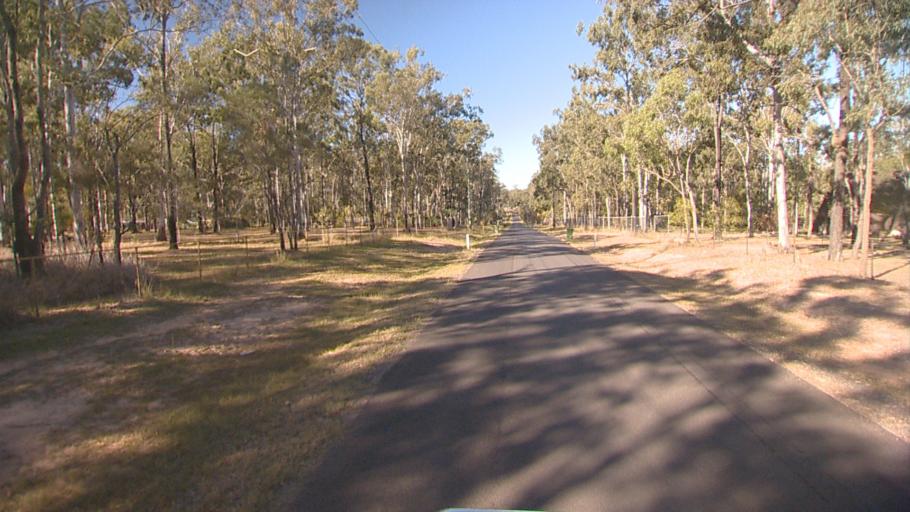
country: AU
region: Queensland
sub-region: Logan
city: Park Ridge South
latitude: -27.7274
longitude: 152.9981
